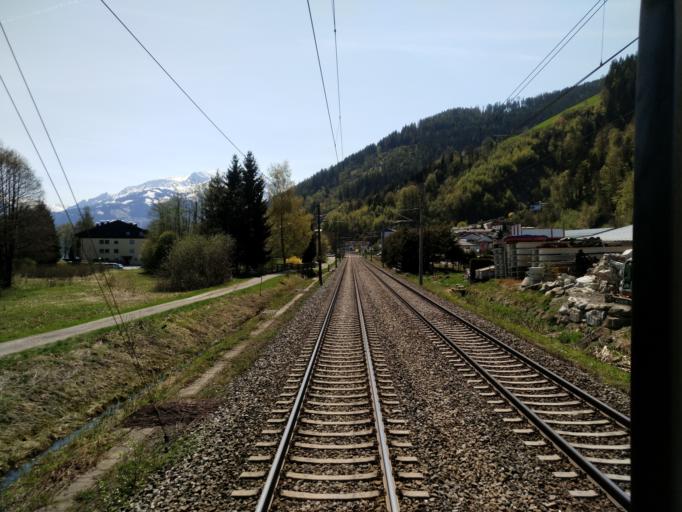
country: AT
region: Salzburg
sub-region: Politischer Bezirk Zell am See
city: Zell am See
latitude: 47.3418
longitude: 12.7998
